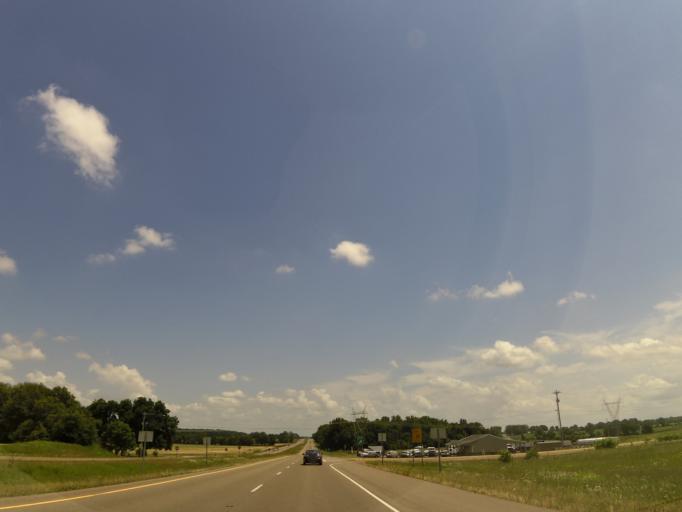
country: US
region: Tennessee
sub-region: Crockett County
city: Alamo
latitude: 35.8825
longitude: -89.2274
